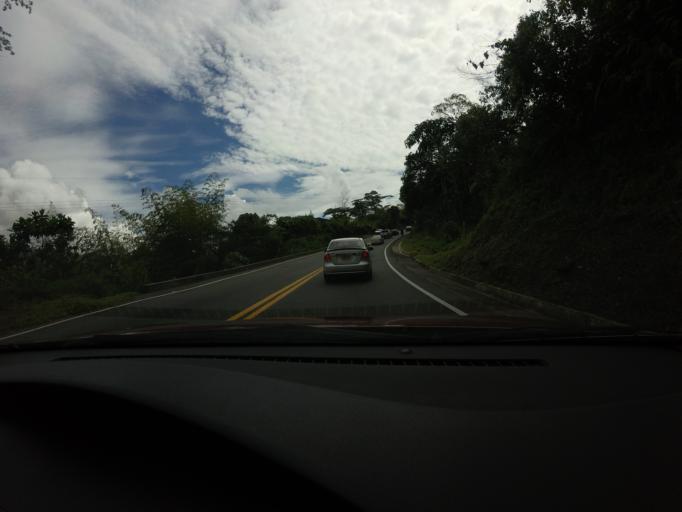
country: CO
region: Antioquia
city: Cocorna
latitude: 6.0377
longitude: -75.1800
